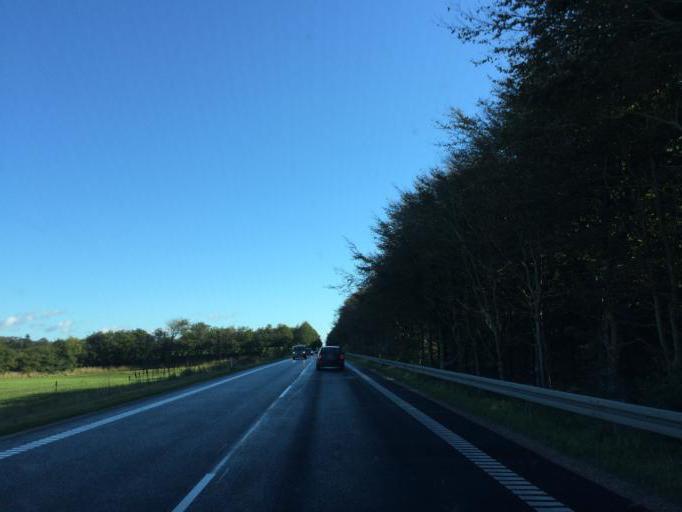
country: DK
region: Central Jutland
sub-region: Viborg Kommune
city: Stoholm
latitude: 56.4253
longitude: 9.0723
